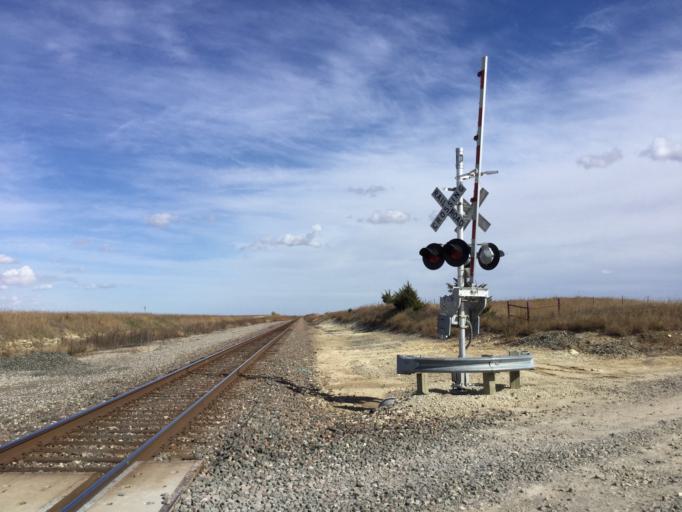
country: US
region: Kansas
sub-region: Butler County
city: El Dorado
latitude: 37.9556
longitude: -96.7193
